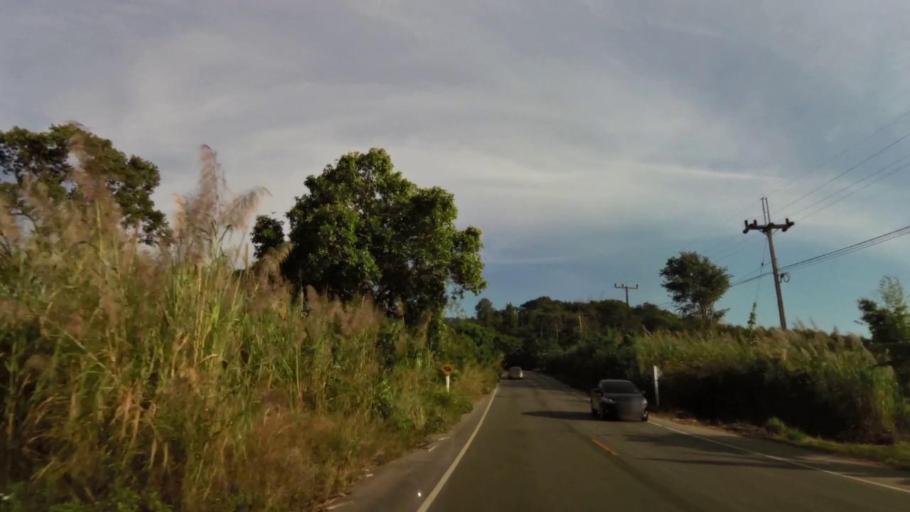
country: TH
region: Chiang Rai
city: Khun Tan
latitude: 19.8639
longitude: 100.4234
